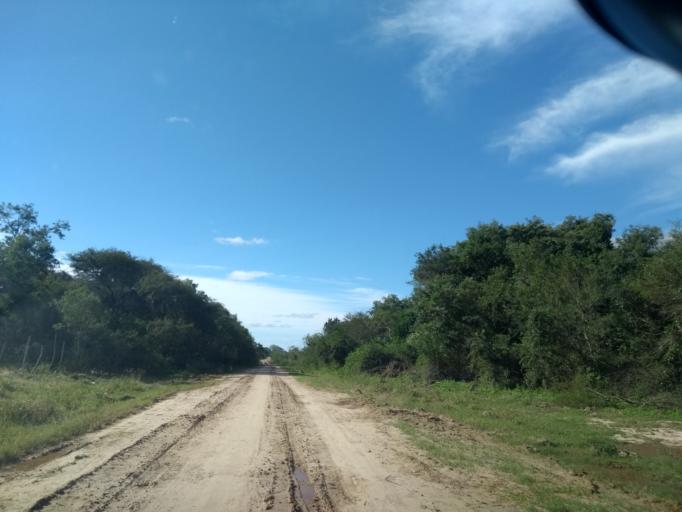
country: AR
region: Chaco
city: Margarita Belen
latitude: -27.2834
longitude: -58.9272
